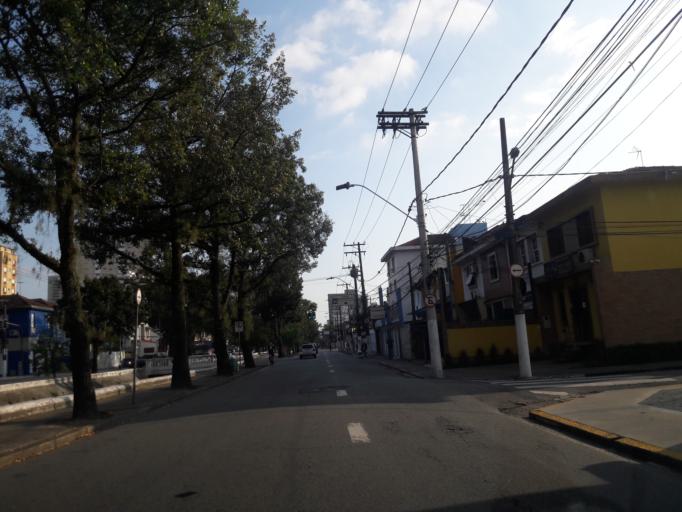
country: BR
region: Sao Paulo
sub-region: Santos
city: Santos
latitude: -23.9497
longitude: -46.3370
